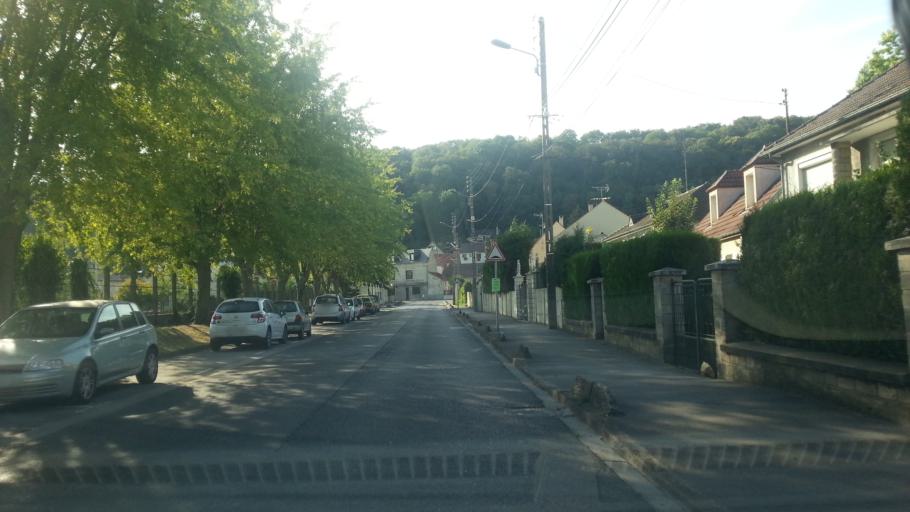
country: FR
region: Picardie
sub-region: Departement de l'Oise
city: Montataire
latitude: 49.2616
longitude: 2.4528
